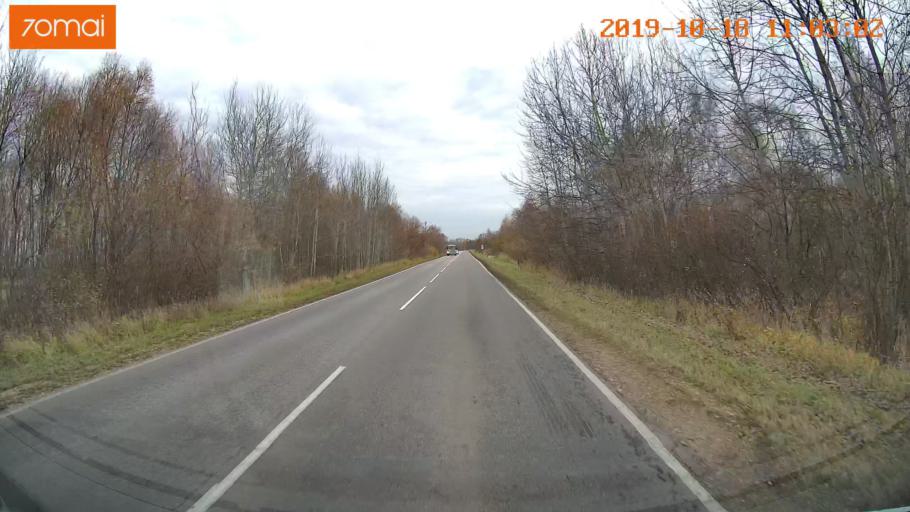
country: RU
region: Tula
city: Yepifan'
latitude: 53.8739
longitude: 38.5456
